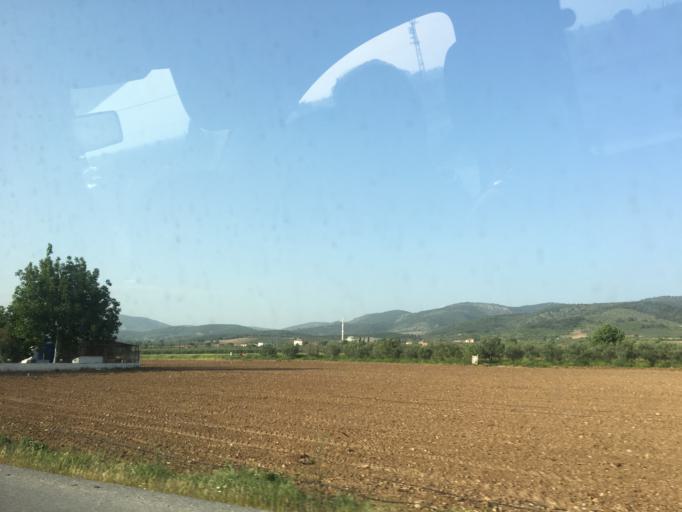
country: TR
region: Manisa
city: Golmarmara
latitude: 38.7887
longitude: 27.9025
